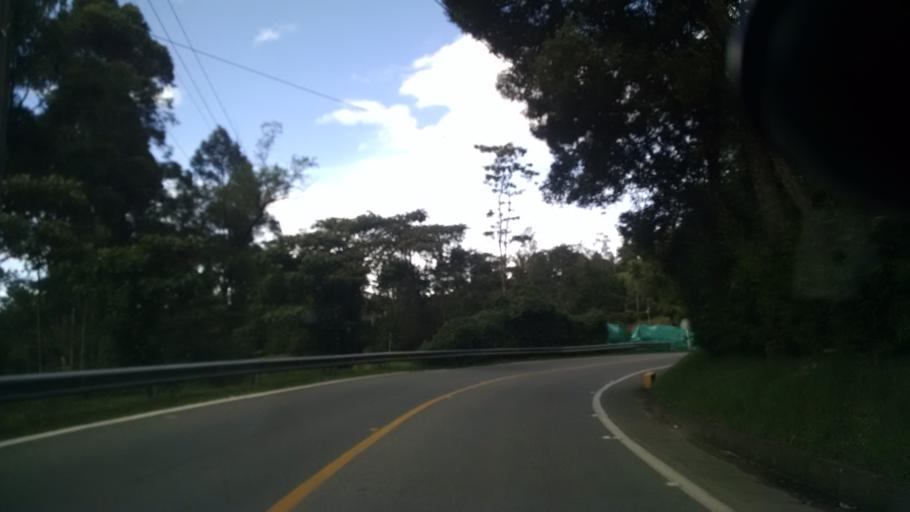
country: CO
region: Antioquia
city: El Retiro
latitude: 6.0813
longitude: -75.4948
